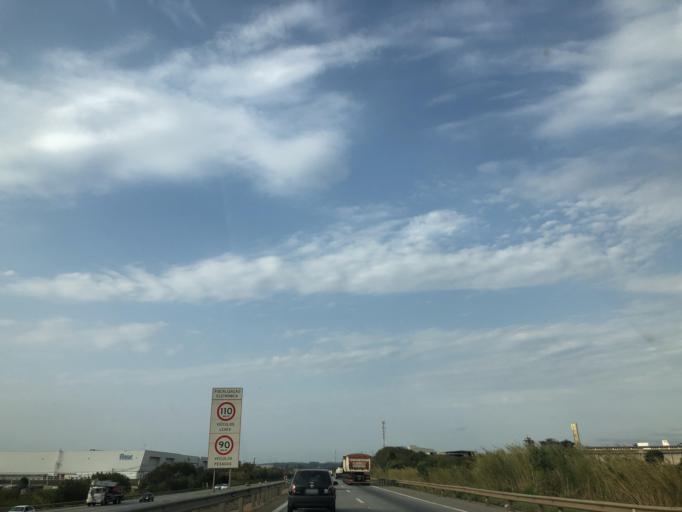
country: BR
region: Sao Paulo
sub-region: Sorocaba
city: Sorocaba
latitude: -23.4323
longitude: -47.3689
